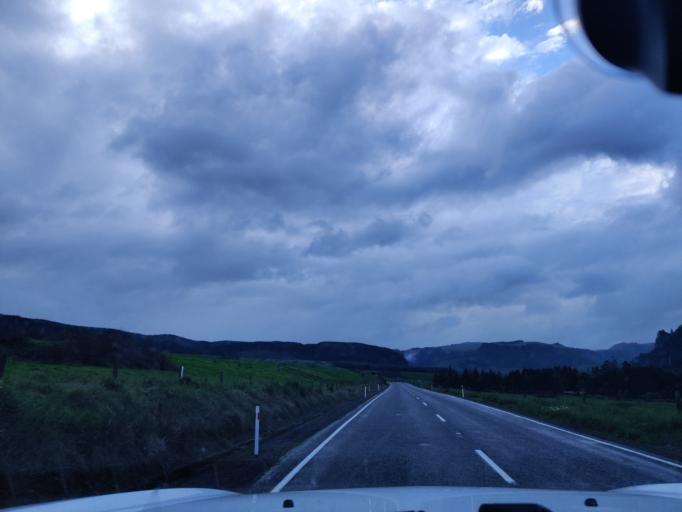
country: NZ
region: Waikato
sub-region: South Waikato District
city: Tokoroa
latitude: -38.4132
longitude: 175.8055
